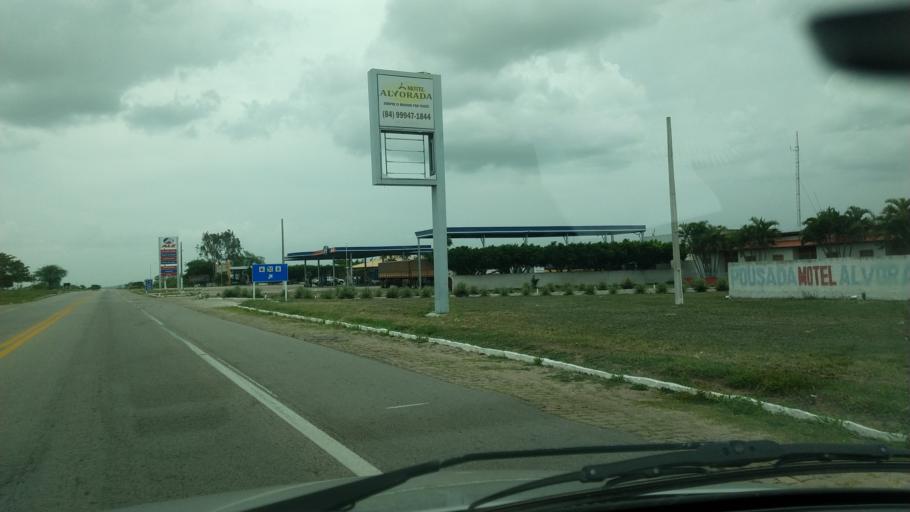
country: BR
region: Rio Grande do Norte
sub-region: Tangara
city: Tangara
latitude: -6.1725
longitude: -35.7640
